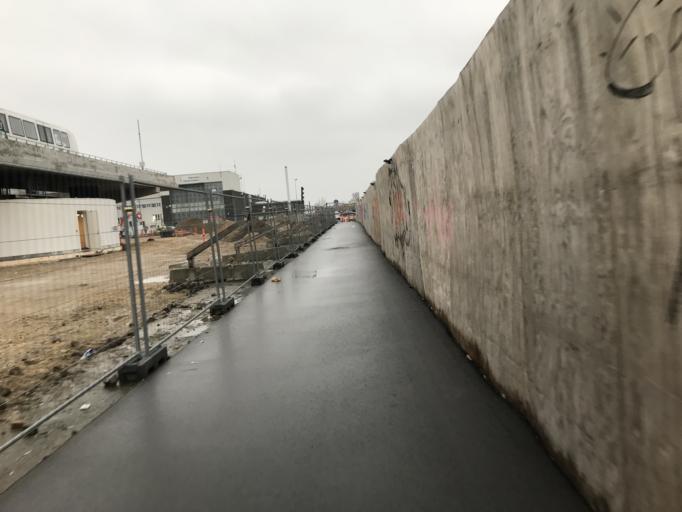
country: DK
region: Capital Region
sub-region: Kobenhavn
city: Christianshavn
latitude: 55.7120
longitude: 12.5957
